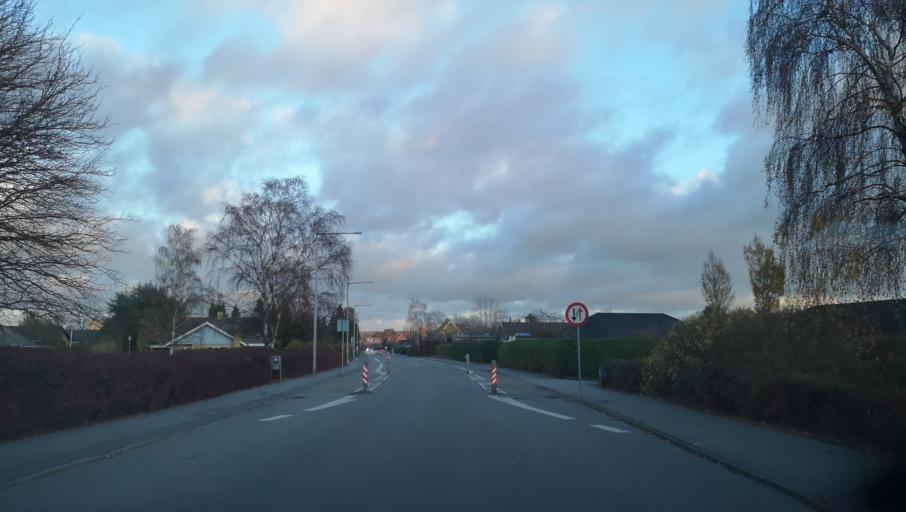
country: DK
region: Zealand
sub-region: Naestved Kommune
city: Naestved
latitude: 55.2280
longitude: 11.7376
